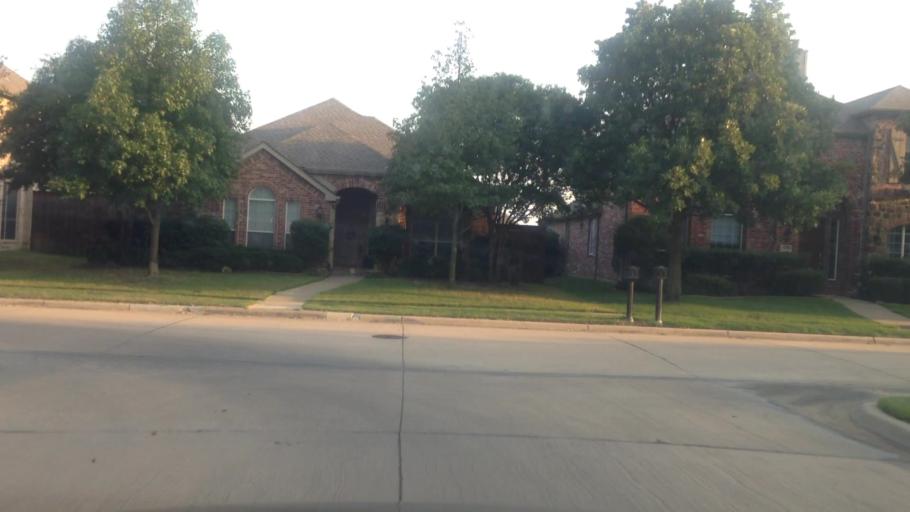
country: US
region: Texas
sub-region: Denton County
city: The Colony
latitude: 33.1238
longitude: -96.8696
